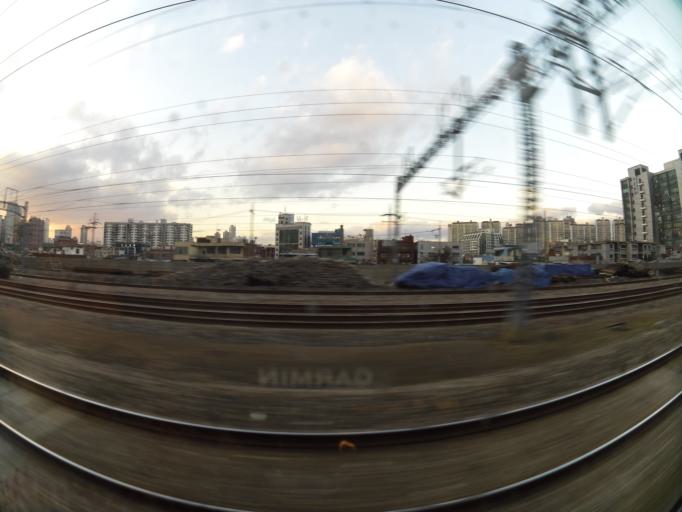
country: KR
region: Gyeonggi-do
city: Kwangmyong
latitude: 37.5106
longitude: 126.8954
